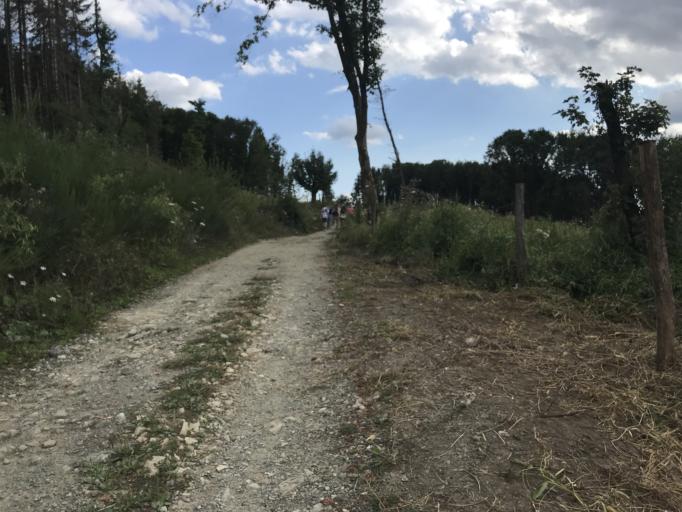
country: IT
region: Emilia-Romagna
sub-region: Provincia di Bologna
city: San Benedetto Val di Sambro
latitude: 44.1514
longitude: 11.2620
